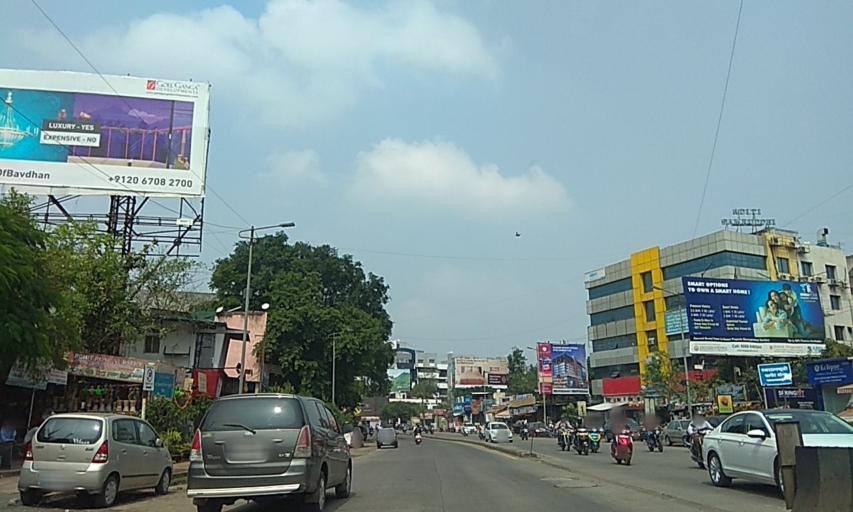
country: IN
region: Maharashtra
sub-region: Pune Division
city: Khadki
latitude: 18.5599
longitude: 73.7897
